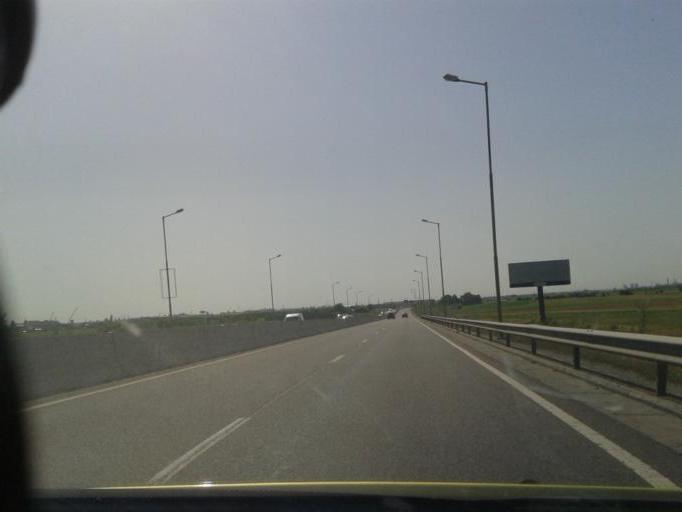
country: RO
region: Prahova
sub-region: Comuna Targsoru Vechi
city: Strejnicu
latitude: 44.9296
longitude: 25.9722
